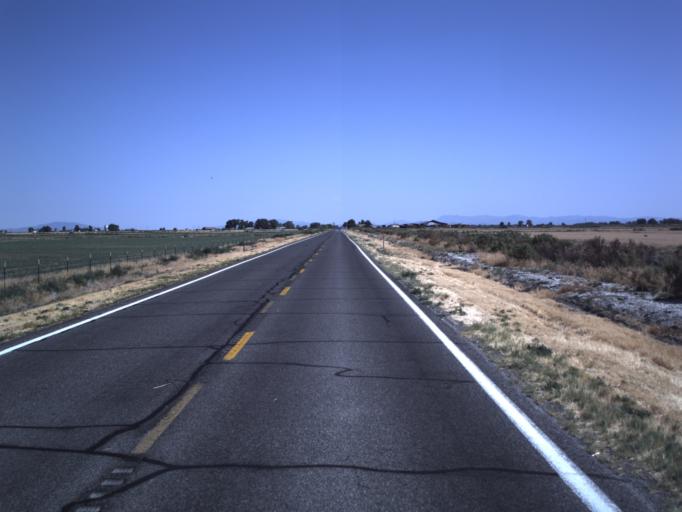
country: US
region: Utah
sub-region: Millard County
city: Delta
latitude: 39.3095
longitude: -112.6525
